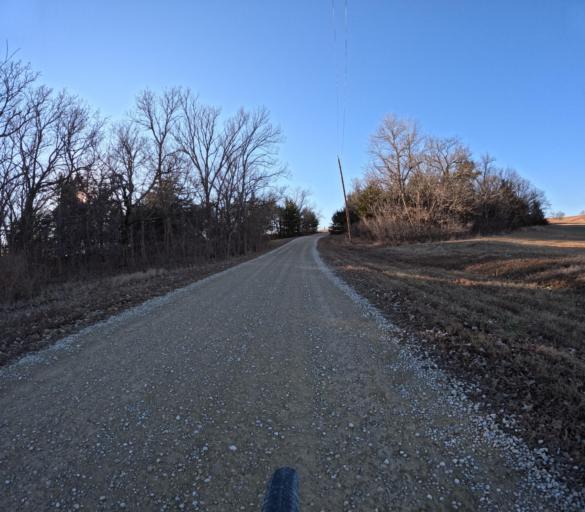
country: US
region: Kansas
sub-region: Riley County
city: Ogden
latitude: 39.2130
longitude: -96.6779
